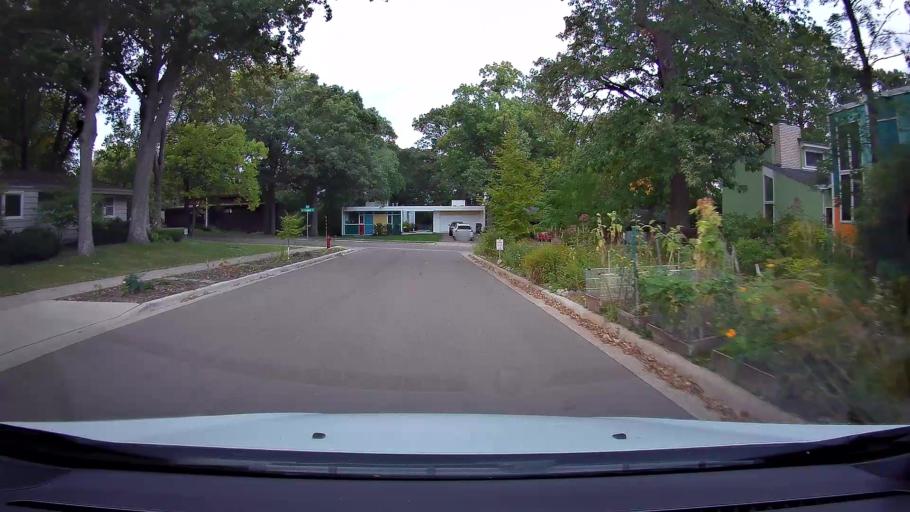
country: US
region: Minnesota
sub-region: Ramsey County
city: Lauderdale
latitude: 44.9890
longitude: -93.1929
